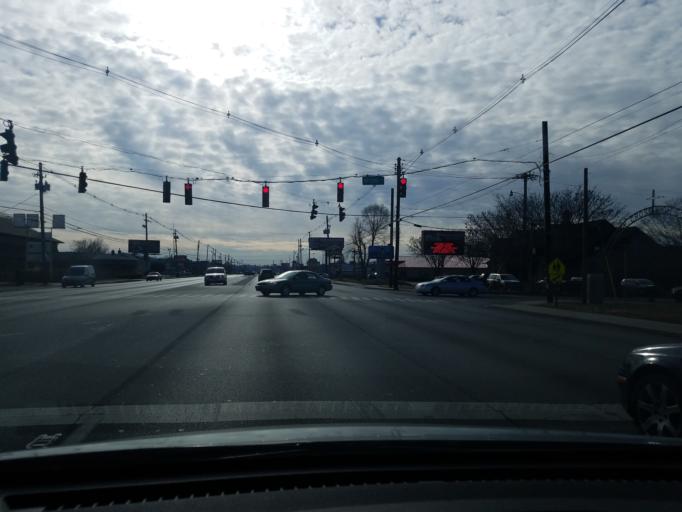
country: US
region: Kentucky
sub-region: Jefferson County
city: Saint Dennis
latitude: 38.1651
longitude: -85.8303
